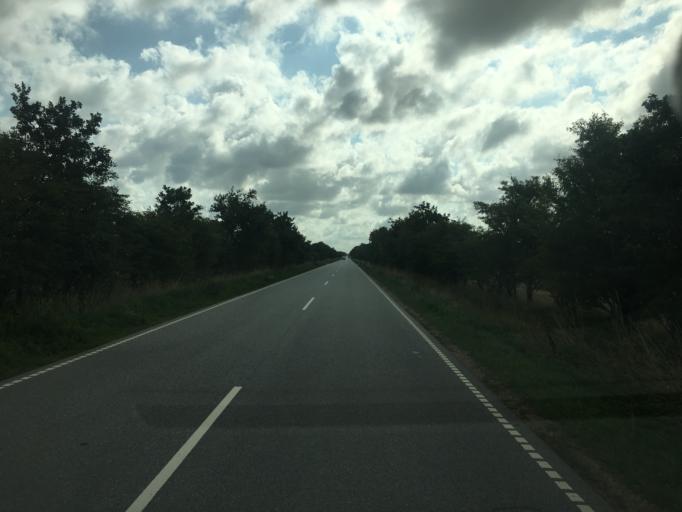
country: DK
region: South Denmark
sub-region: Tonder Kommune
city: Sherrebek
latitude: 55.1245
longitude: 8.8180
